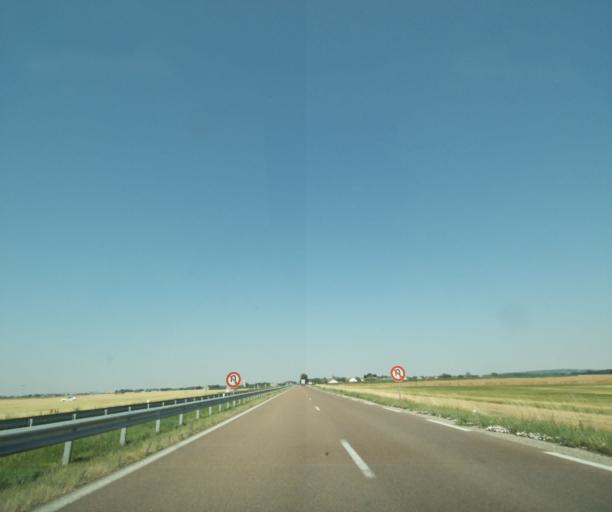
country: FR
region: Champagne-Ardenne
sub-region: Departement de la Marne
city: Frignicourt
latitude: 48.7021
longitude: 4.6732
